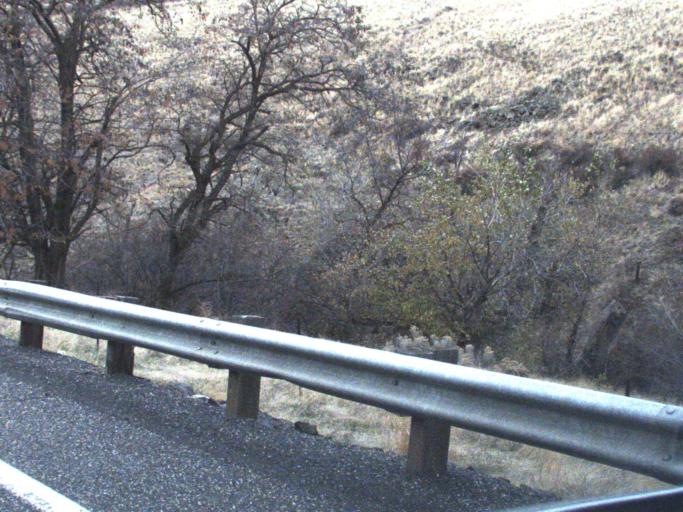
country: US
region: Washington
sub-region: Garfield County
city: Pomeroy
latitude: 46.4466
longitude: -117.4522
